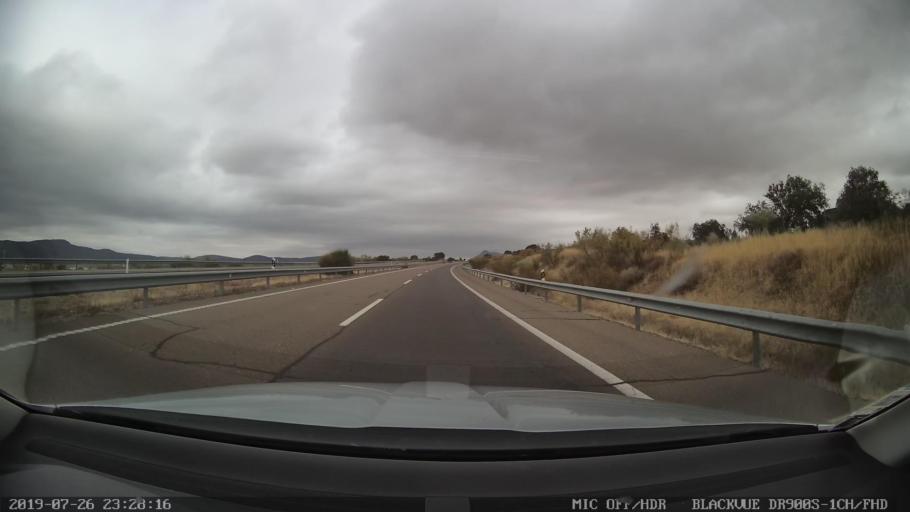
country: ES
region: Extremadura
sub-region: Provincia de Caceres
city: Villamesias
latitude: 39.2435
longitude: -5.8824
